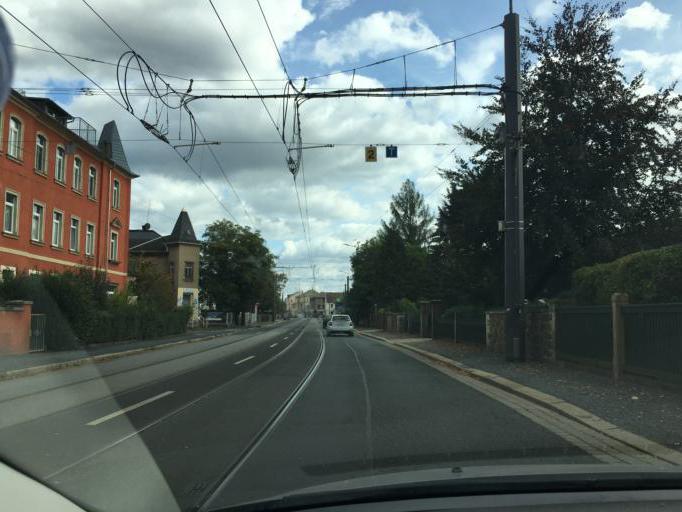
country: DE
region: Saxony
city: Radebeul
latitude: 51.1092
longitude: 13.6266
